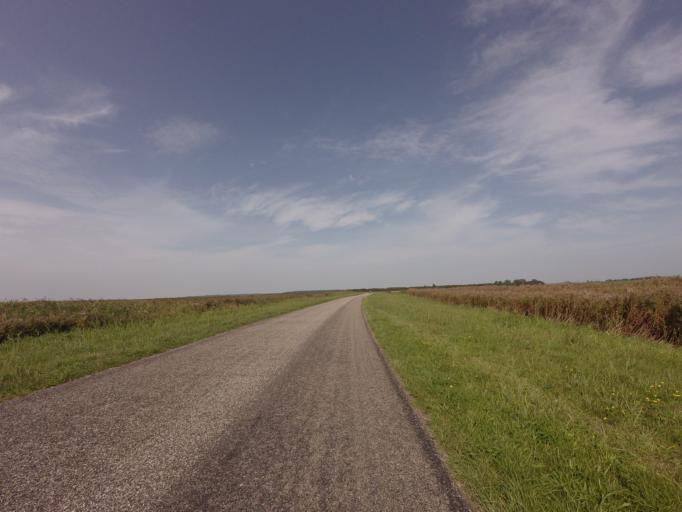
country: NL
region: Groningen
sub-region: Gemeente De Marne
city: Ulrum
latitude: 53.3494
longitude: 6.2667
